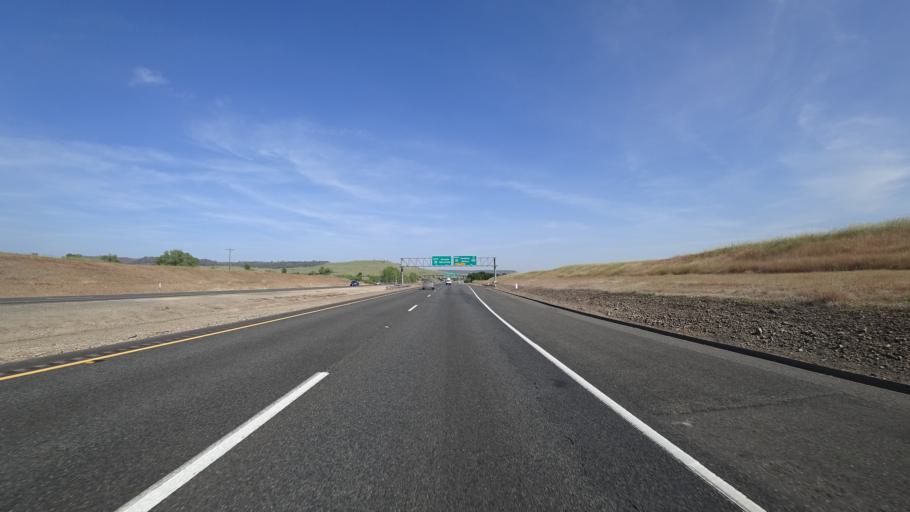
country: US
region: California
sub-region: Butte County
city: Thermalito
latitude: 39.5880
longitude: -121.6338
